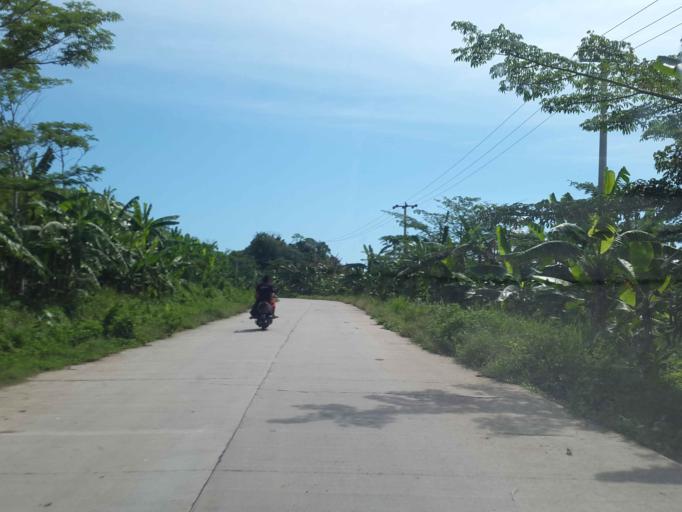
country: ID
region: Banten
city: Babakanbungur
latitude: -6.5243
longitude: 105.6288
